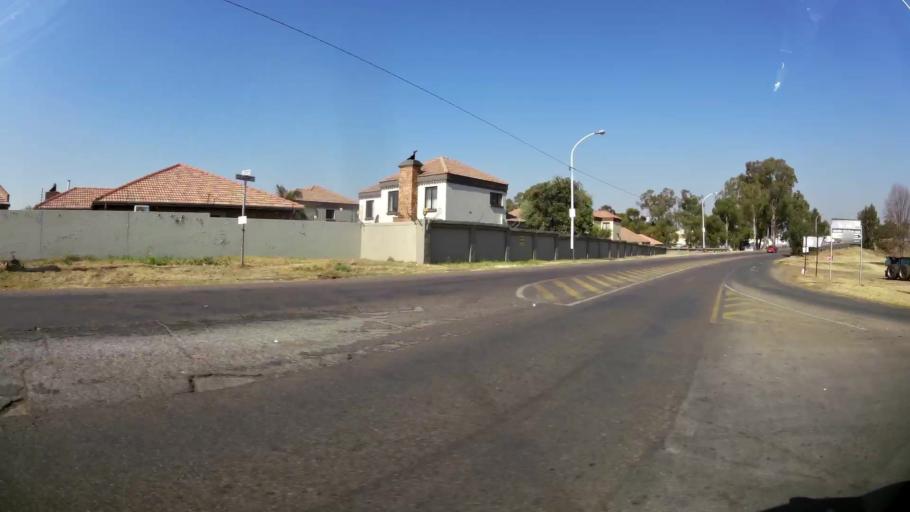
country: ZA
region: Gauteng
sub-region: Ekurhuleni Metropolitan Municipality
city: Boksburg
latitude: -26.1711
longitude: 28.2731
